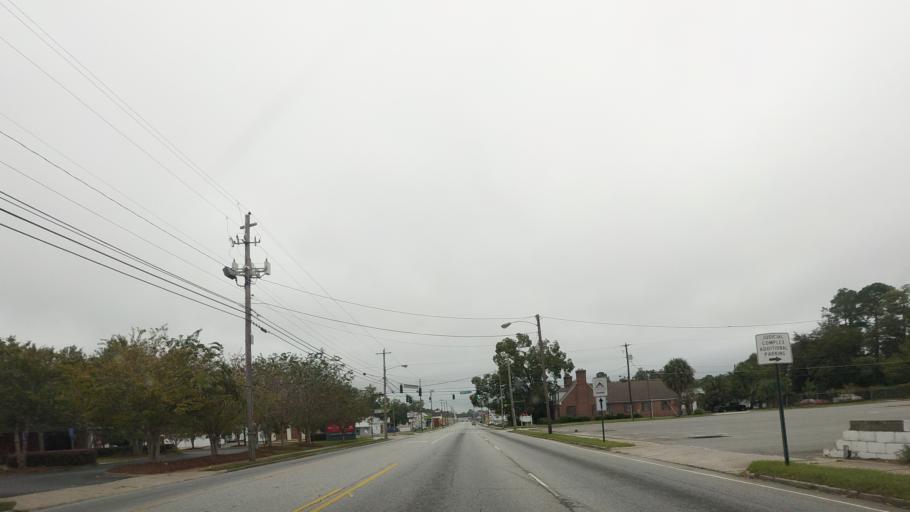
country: US
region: Georgia
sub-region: Lowndes County
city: Valdosta
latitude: 30.8363
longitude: -83.2795
